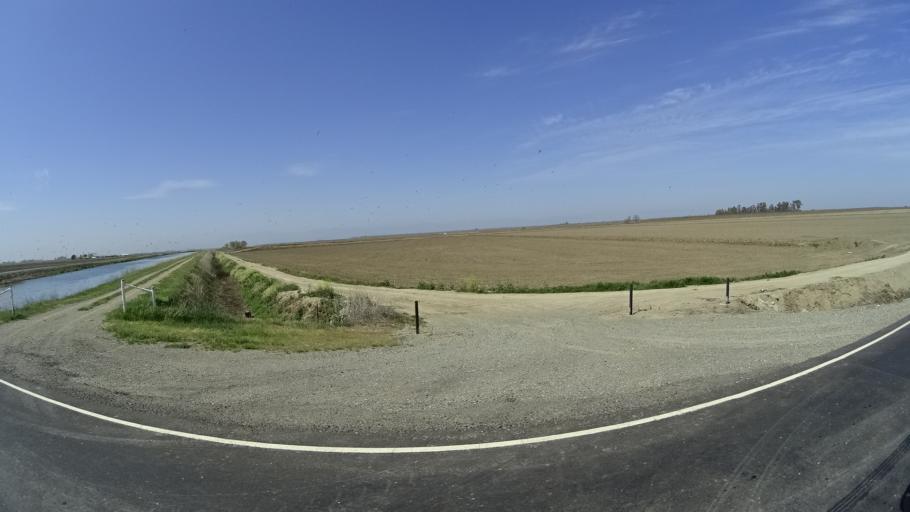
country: US
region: California
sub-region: Glenn County
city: Hamilton City
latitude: 39.6269
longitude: -122.0652
